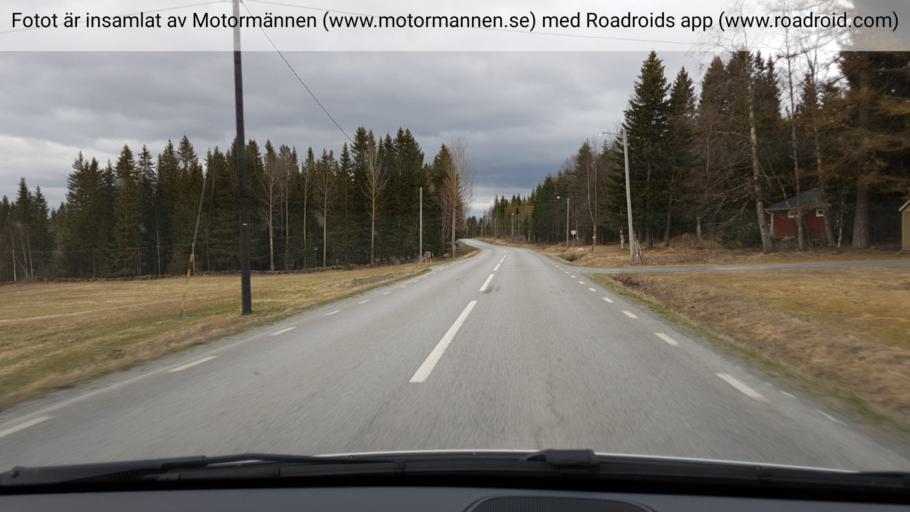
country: SE
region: Jaemtland
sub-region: Krokoms Kommun
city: Krokom
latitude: 63.1525
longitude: 14.1539
